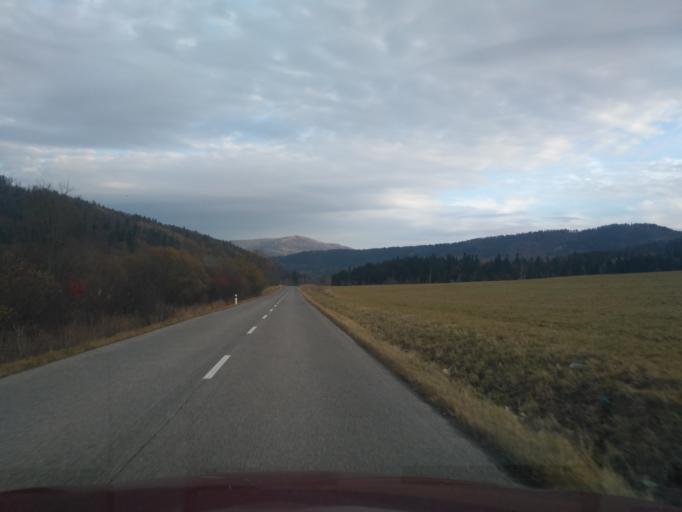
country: SK
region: Kosicky
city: Krompachy
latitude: 48.8006
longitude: 20.7357
